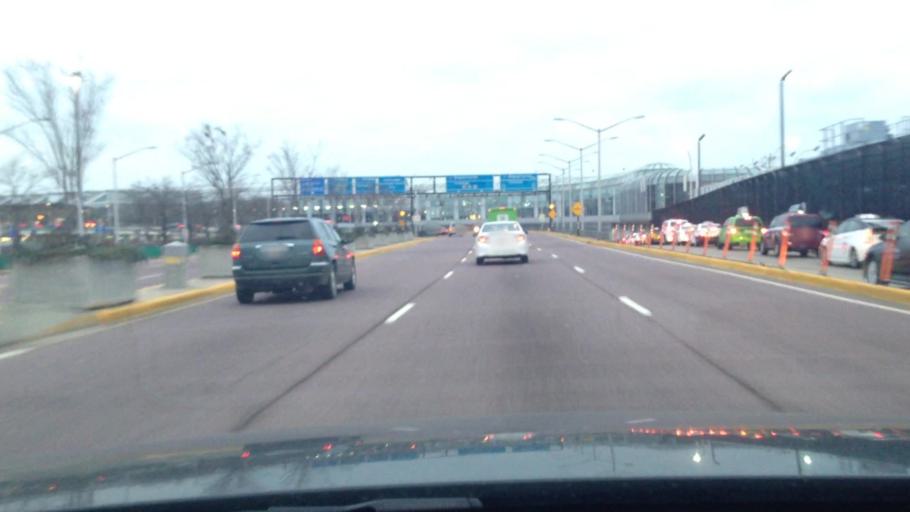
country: US
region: Illinois
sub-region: Cook County
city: Rosemont
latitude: 41.9819
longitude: -87.9032
